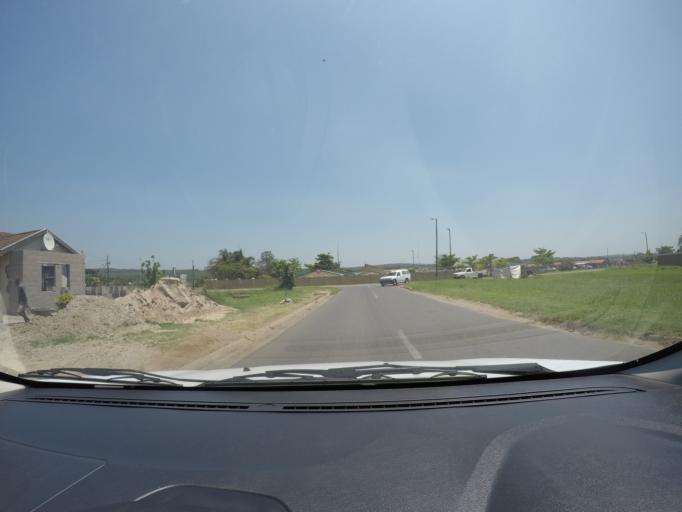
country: ZA
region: KwaZulu-Natal
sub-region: uThungulu District Municipality
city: eSikhawini
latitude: -28.8696
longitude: 31.9099
